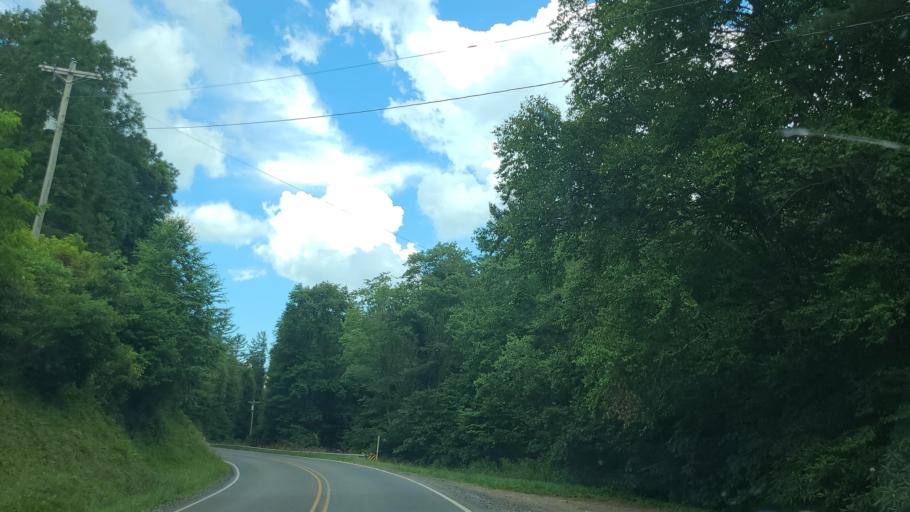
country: US
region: North Carolina
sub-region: Ashe County
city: Jefferson
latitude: 36.3946
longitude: -81.3686
